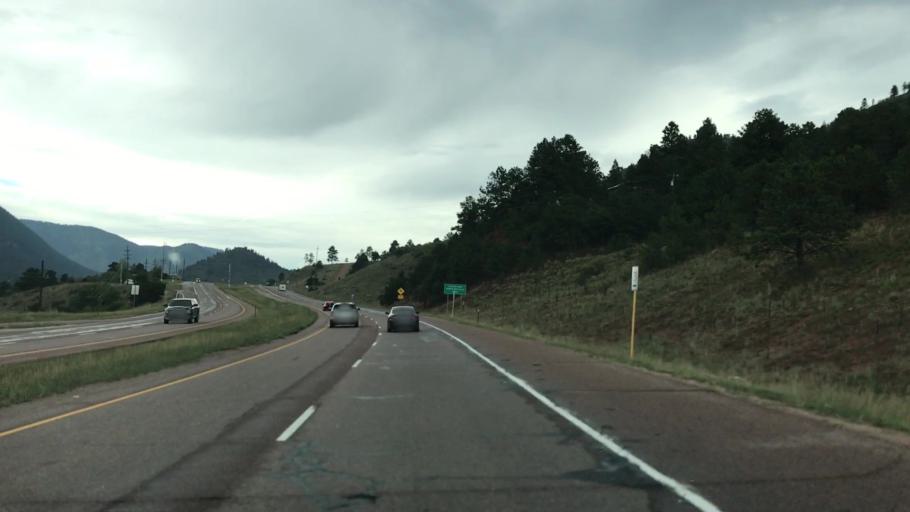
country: US
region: Colorado
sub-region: El Paso County
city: Cascade-Chipita Park
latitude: 38.9187
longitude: -104.9847
